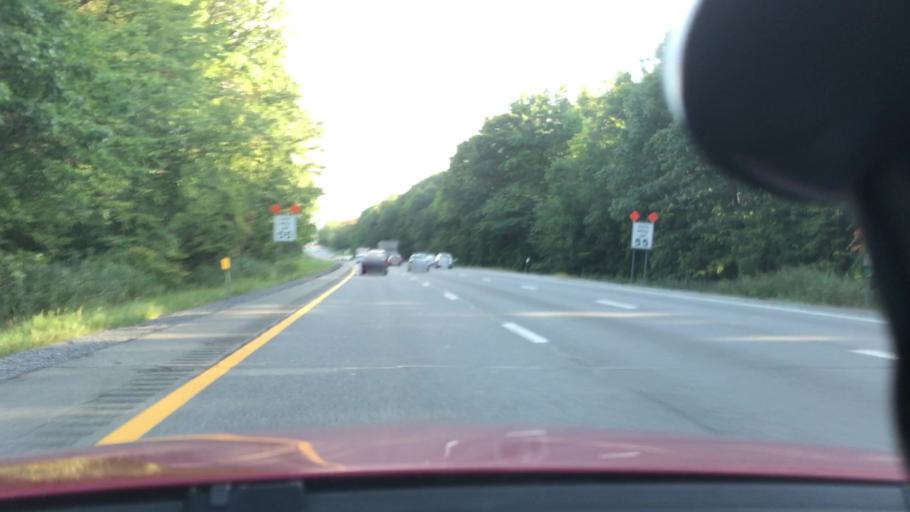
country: US
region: New York
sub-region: Albany County
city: Cohoes
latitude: 42.8119
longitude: -73.7672
